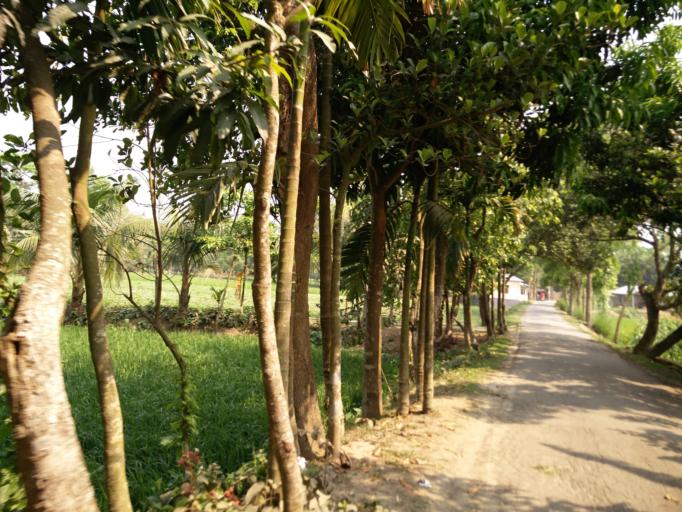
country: BD
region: Dhaka
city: Muktagacha
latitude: 24.9258
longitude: 90.2473
